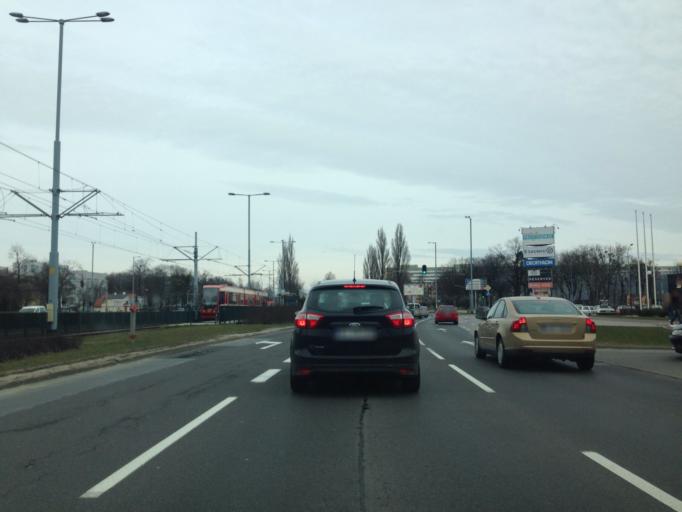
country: PL
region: Pomeranian Voivodeship
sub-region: Sopot
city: Sopot
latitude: 54.4073
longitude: 18.5896
